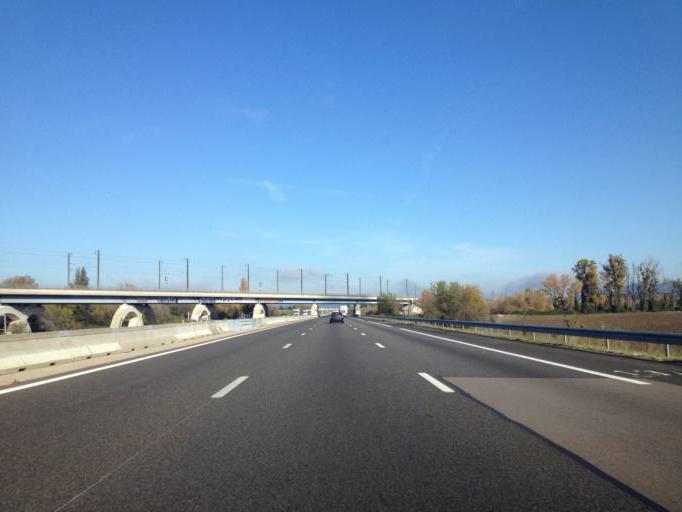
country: FR
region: Rhone-Alpes
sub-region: Departement de la Drome
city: Pierrelatte
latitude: 44.3755
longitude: 4.7328
